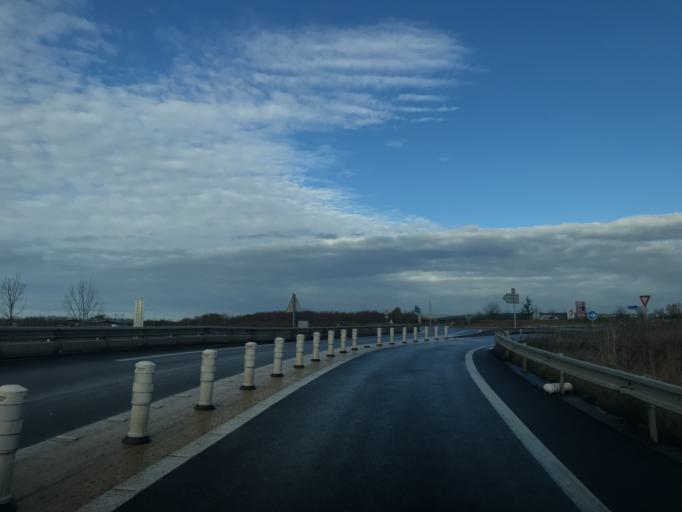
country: FR
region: Lower Normandy
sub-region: Departement de l'Orne
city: Valframbert
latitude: 48.4519
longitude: 0.1291
